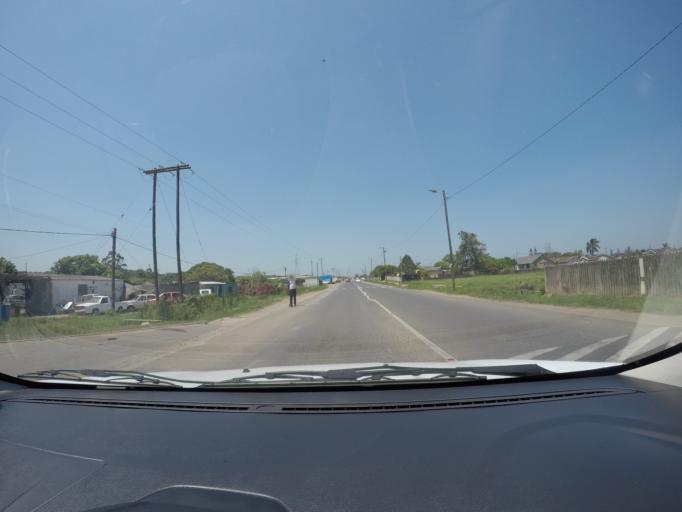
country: ZA
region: KwaZulu-Natal
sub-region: uThungulu District Municipality
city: eSikhawini
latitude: -28.8631
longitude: 31.9119
